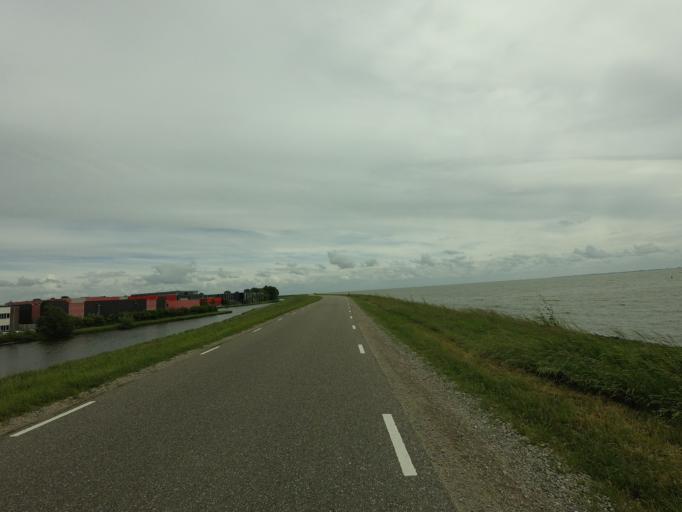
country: NL
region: North Holland
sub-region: Gemeente Hoorn
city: Hoorn
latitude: 52.6391
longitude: 5.0946
